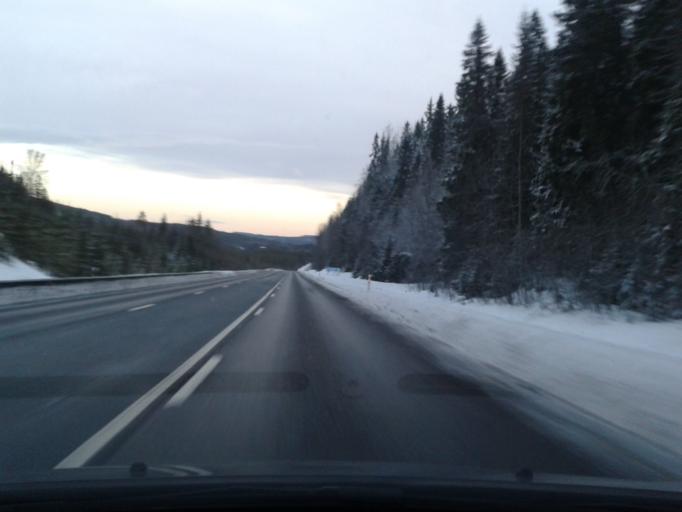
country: SE
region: Vaesternorrland
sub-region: Kramfors Kommun
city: Bollstabruk
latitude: 63.1131
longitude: 17.4980
